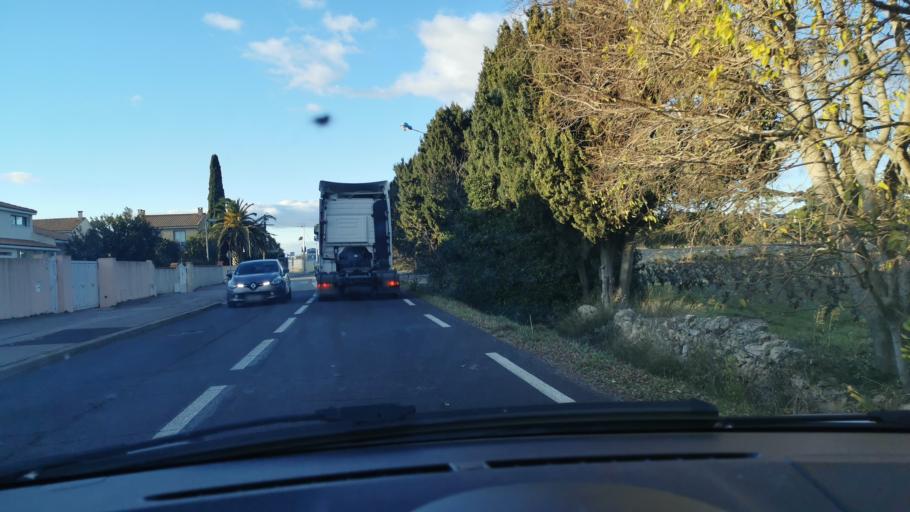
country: FR
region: Languedoc-Roussillon
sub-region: Departement de l'Herault
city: Frontignan
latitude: 43.4334
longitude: 3.7221
